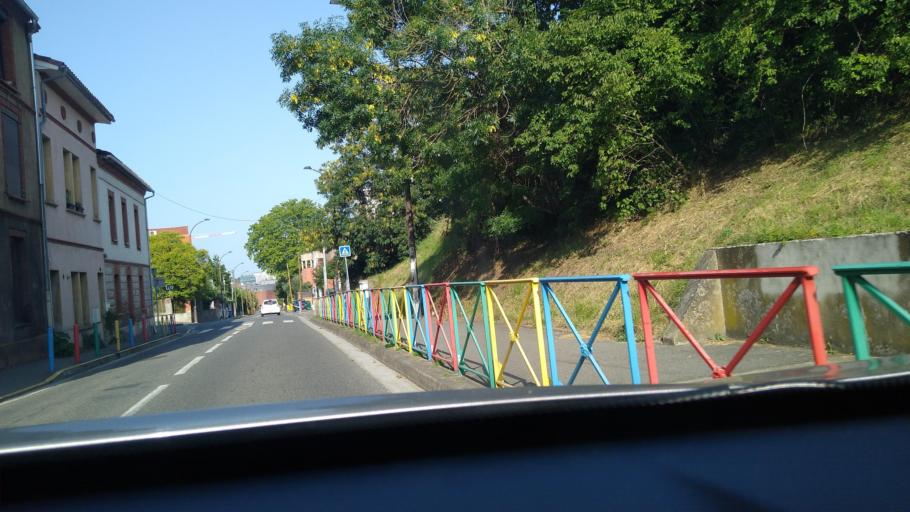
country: FR
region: Midi-Pyrenees
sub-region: Departement de la Haute-Garonne
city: Toulouse
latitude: 43.6178
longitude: 1.4603
